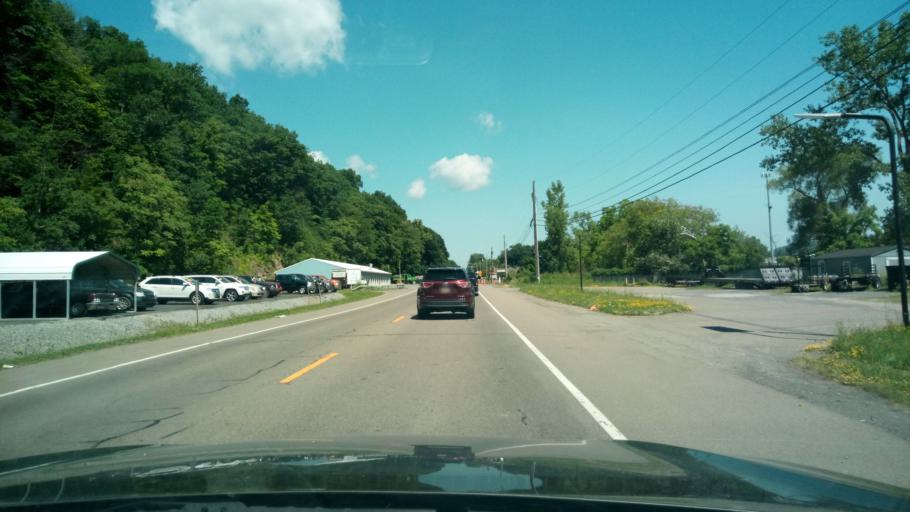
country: US
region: New York
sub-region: Schuyler County
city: Watkins Glen
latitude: 42.3662
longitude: -76.8658
